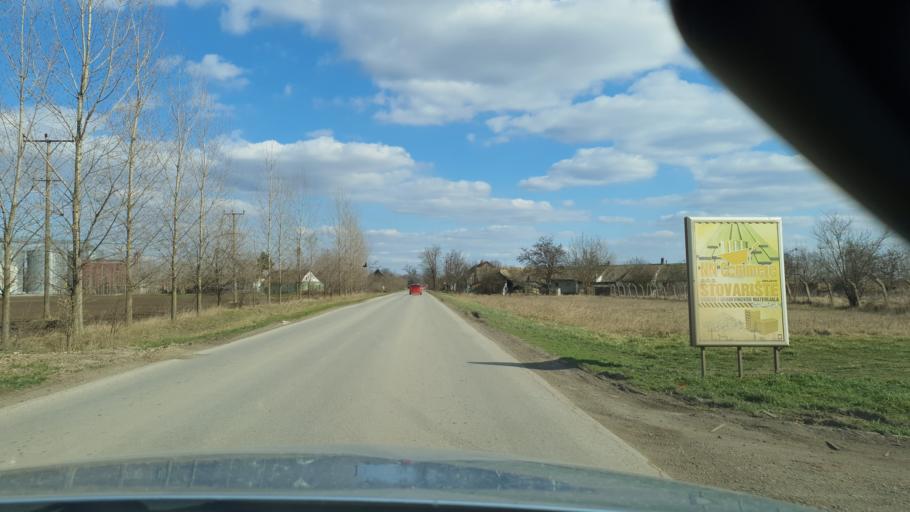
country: RS
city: Zmajevo
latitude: 45.4586
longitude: 19.6685
